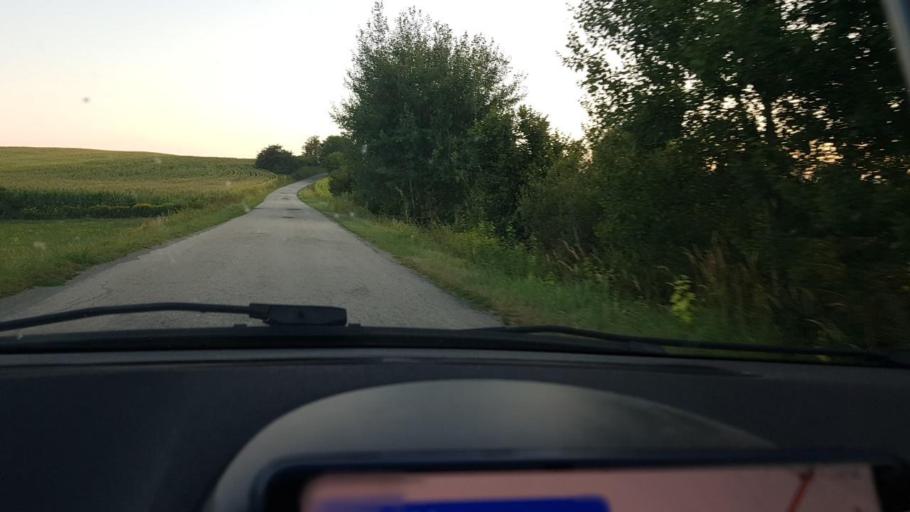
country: HR
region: Bjelovarsko-Bilogorska
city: Zdralovi
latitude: 45.8643
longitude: 16.9970
